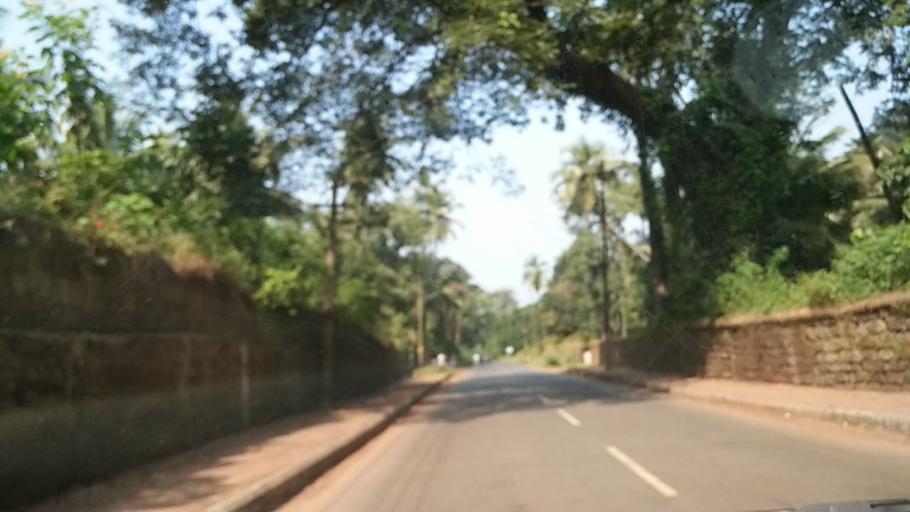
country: IN
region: Goa
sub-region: North Goa
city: Jua
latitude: 15.5023
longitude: 73.9086
